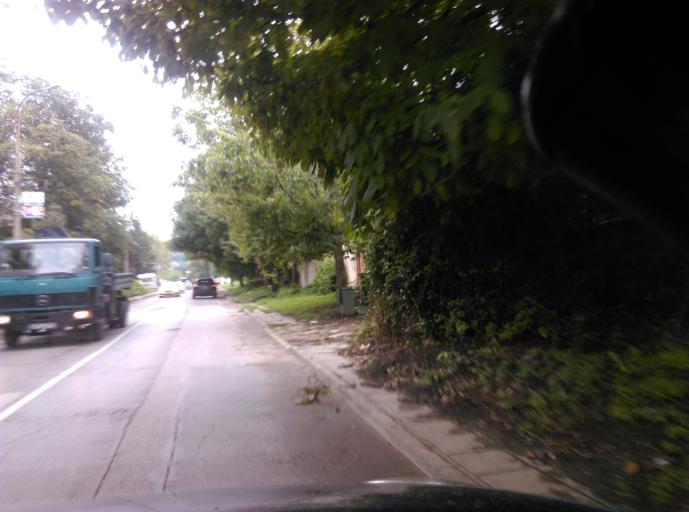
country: BG
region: Sofia-Capital
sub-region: Stolichna Obshtina
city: Sofia
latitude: 42.6277
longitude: 23.3169
